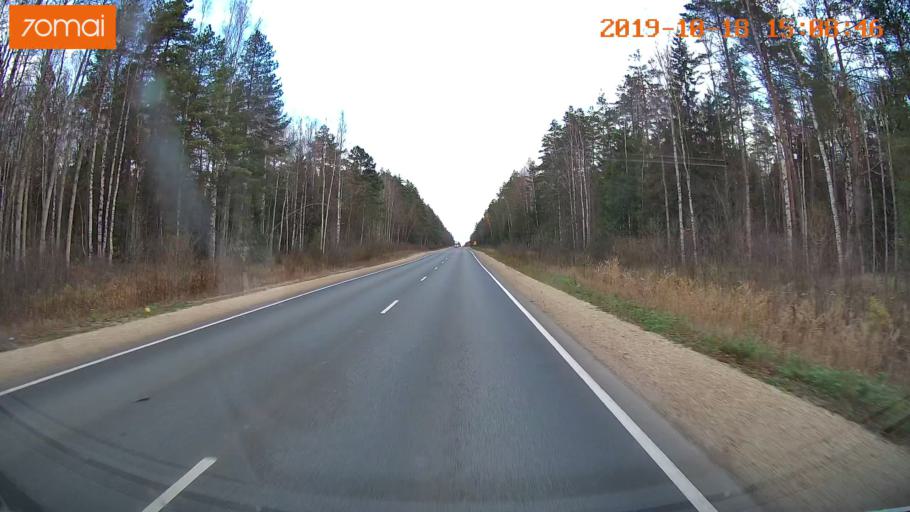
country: RU
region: Vladimir
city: Gus'-Khrustal'nyy
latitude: 55.5568
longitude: 40.6139
